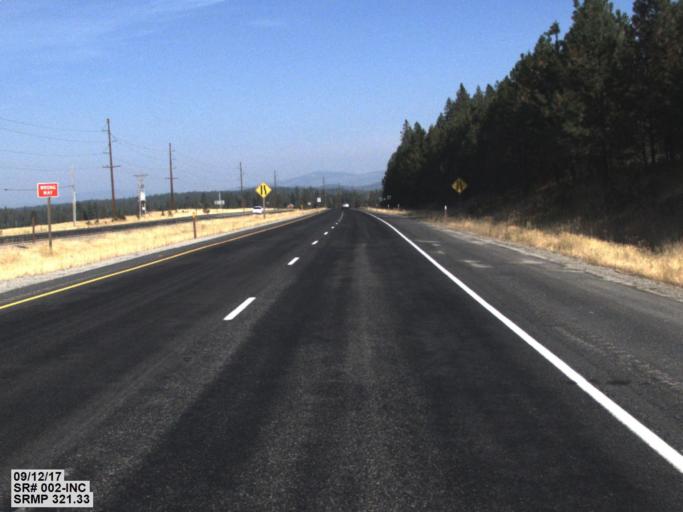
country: US
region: Washington
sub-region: Spokane County
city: Deer Park
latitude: 48.0970
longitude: -117.2782
